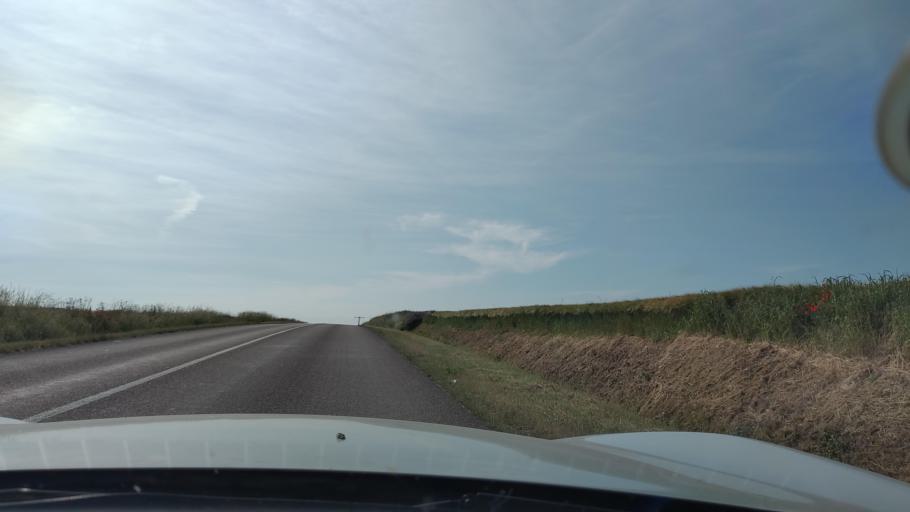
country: FR
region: Champagne-Ardenne
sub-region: Departement de l'Aube
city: Nogent-sur-Seine
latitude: 48.4898
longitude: 3.5240
